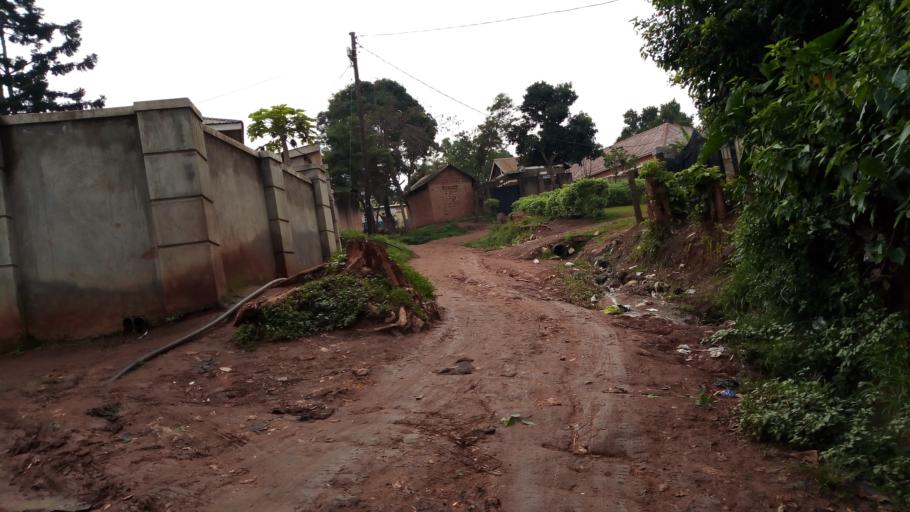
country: UG
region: Central Region
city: Kampala Central Division
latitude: 0.3692
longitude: 32.5556
